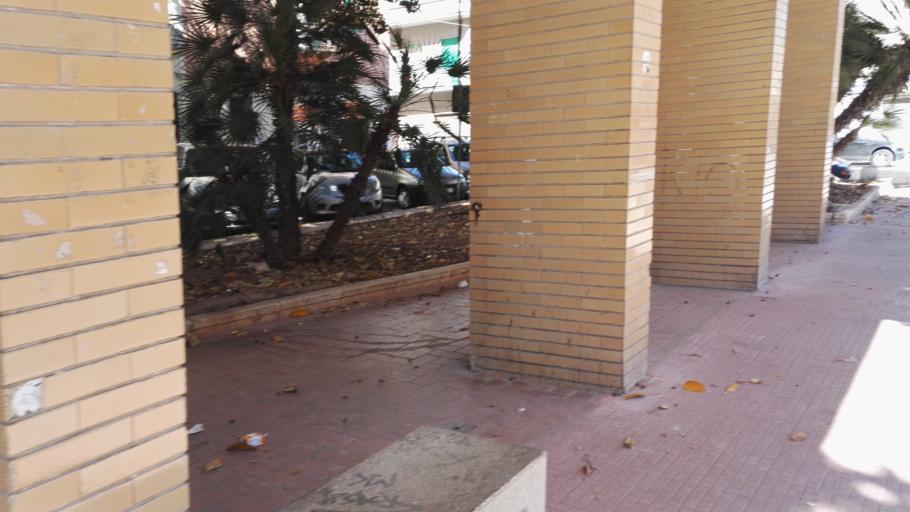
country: IT
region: Sicily
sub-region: Trapani
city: Marsala
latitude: 37.7964
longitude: 12.4353
